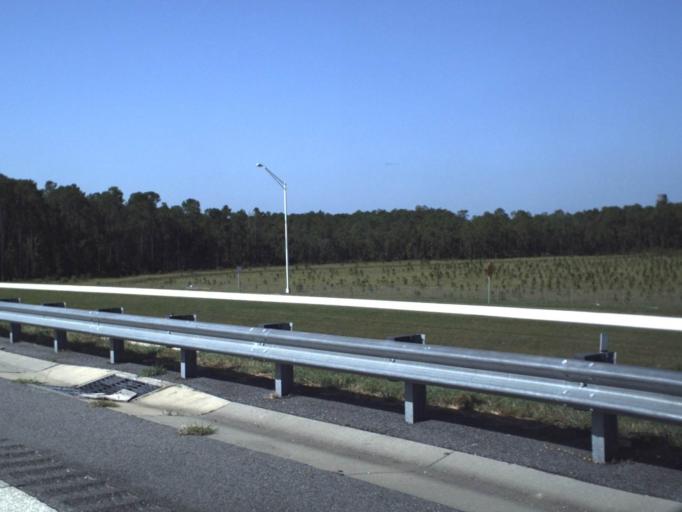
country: US
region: Florida
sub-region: Saint Johns County
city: Palm Valley
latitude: 30.1652
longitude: -81.5112
